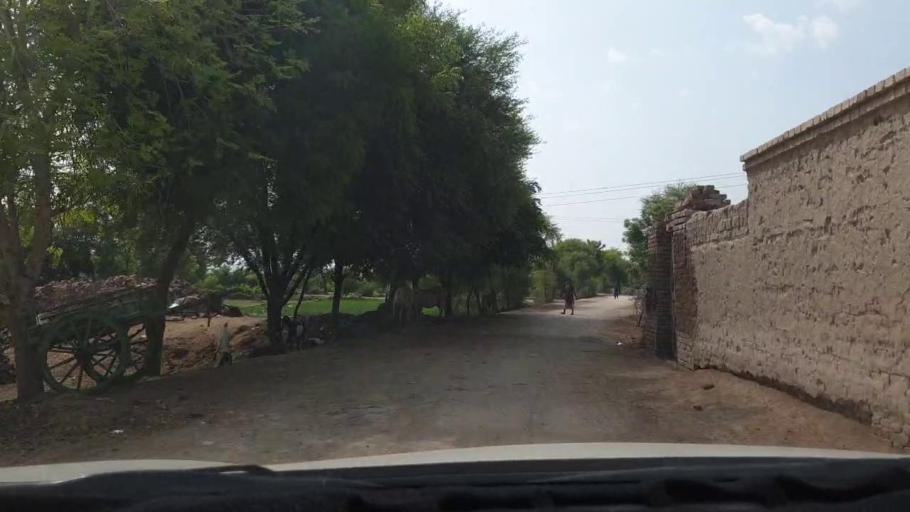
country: PK
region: Sindh
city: Dokri
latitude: 27.3883
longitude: 68.1222
